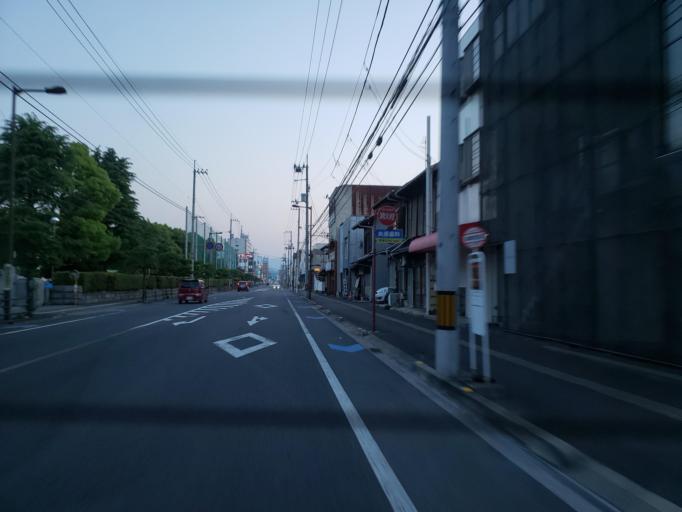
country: JP
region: Ehime
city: Hojo
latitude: 34.0564
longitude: 132.9891
